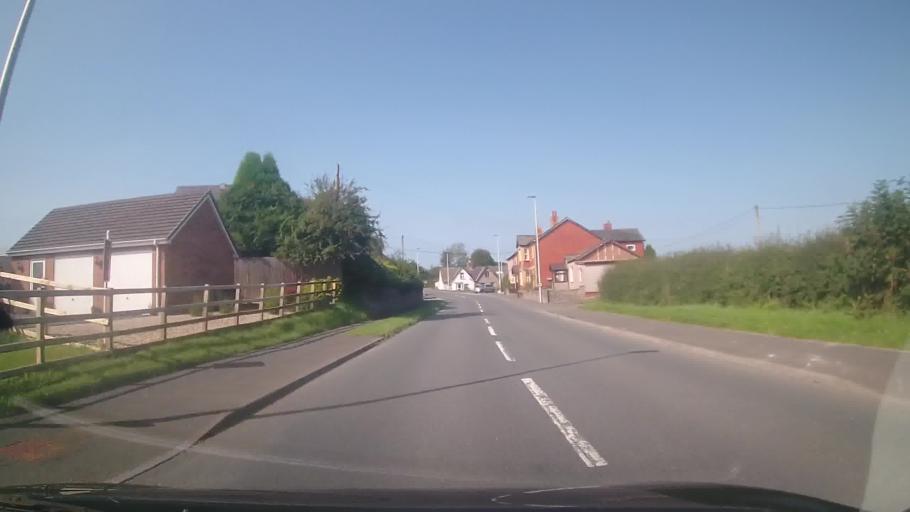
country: GB
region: Wales
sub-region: Sir Powys
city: Builth Wells
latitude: 52.1524
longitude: -3.4560
